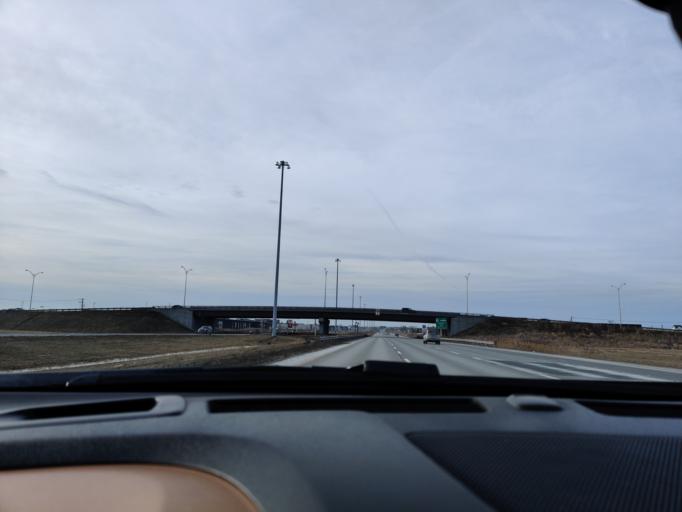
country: CA
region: Quebec
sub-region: Monteregie
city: Vaudreuil-Dorion
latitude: 45.4112
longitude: -74.0356
